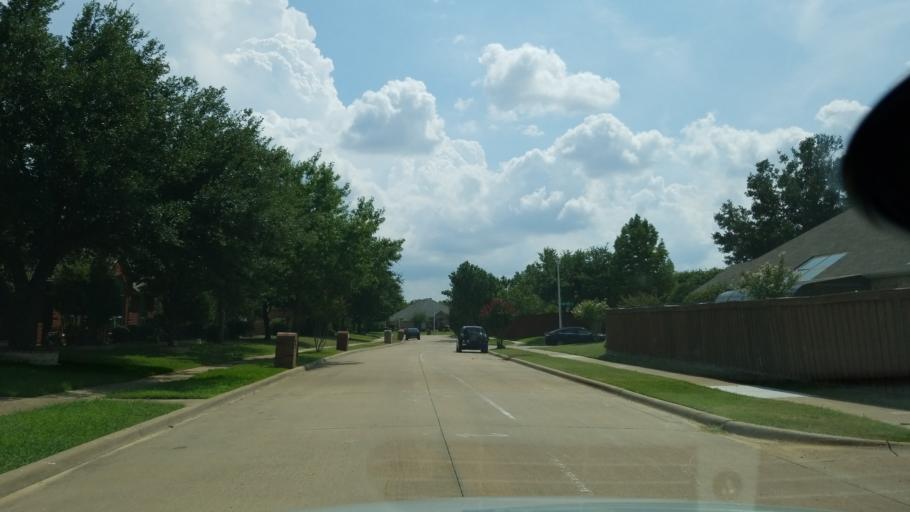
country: US
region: Texas
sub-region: Dallas County
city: Garland
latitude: 32.9231
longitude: -96.6587
